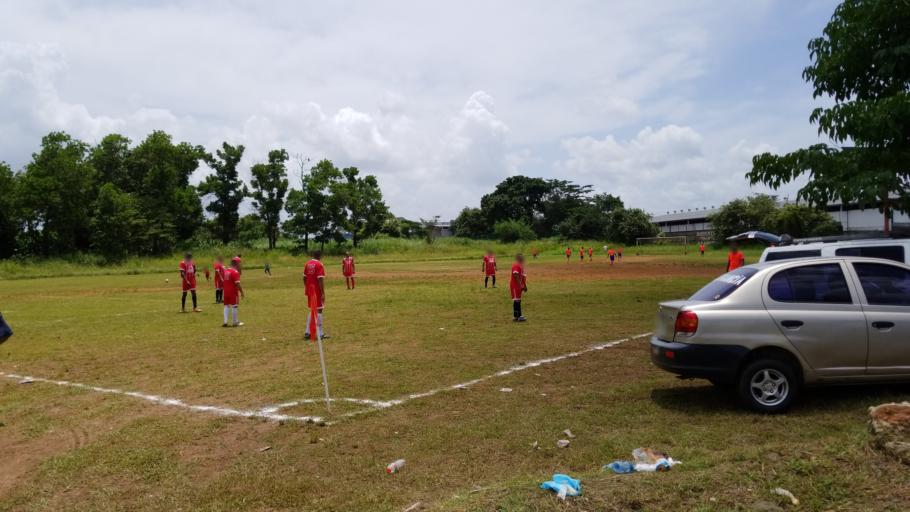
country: PA
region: Panama
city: San Miguelito
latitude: 9.0440
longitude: -79.4405
